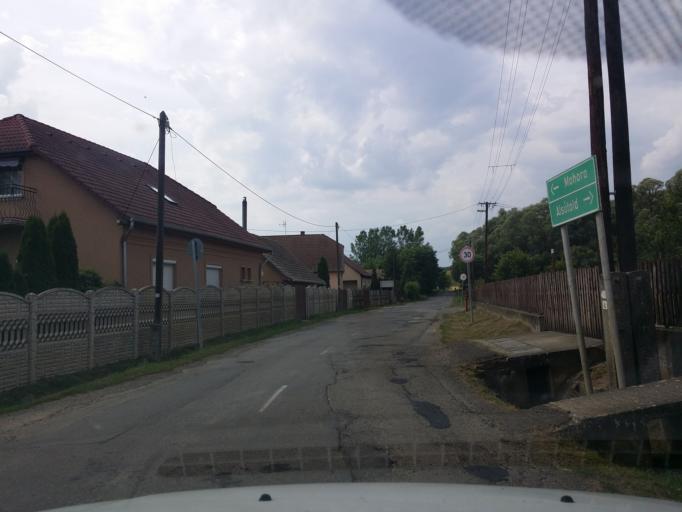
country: HU
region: Nograd
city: Balassagyarmat
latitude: 47.9833
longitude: 19.3707
